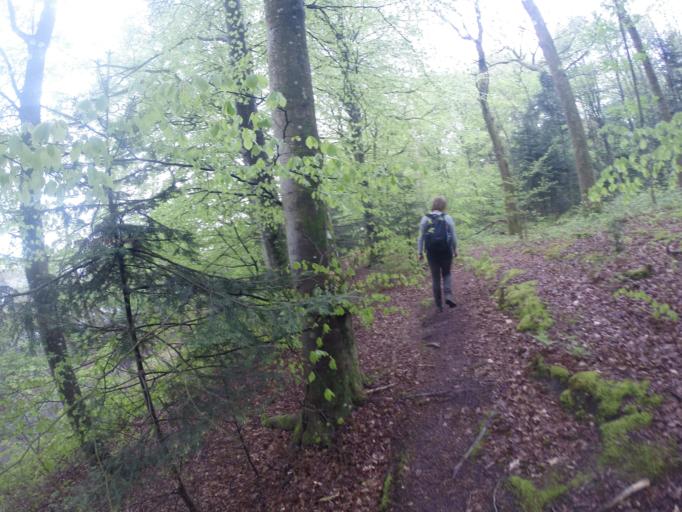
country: DK
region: North Denmark
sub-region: Thisted Kommune
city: Hanstholm
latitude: 57.0303
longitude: 8.5935
